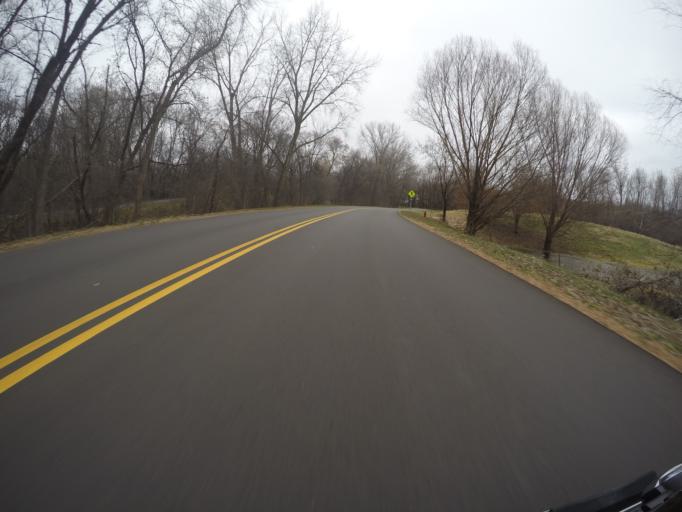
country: US
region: Minnesota
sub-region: Hennepin County
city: Eden Prairie
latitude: 44.8730
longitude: -93.4697
